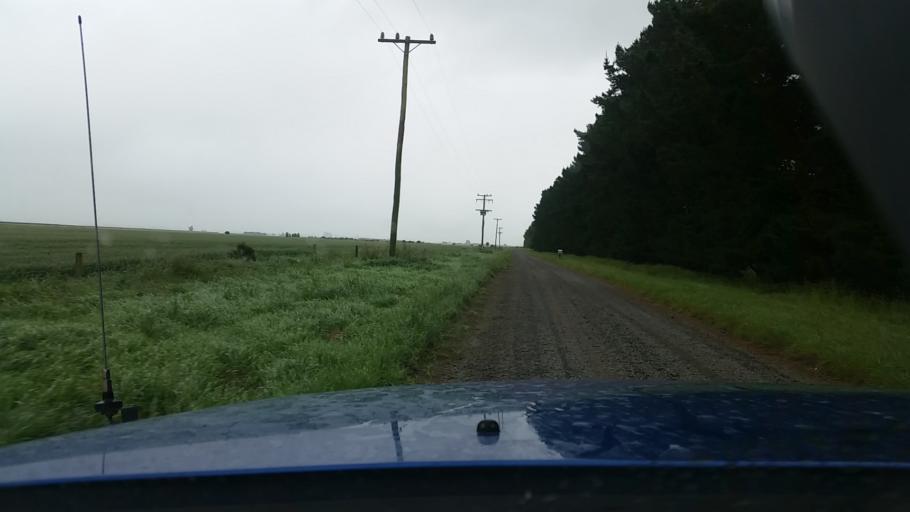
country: NZ
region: Canterbury
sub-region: Ashburton District
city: Tinwald
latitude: -44.0561
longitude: 171.7392
